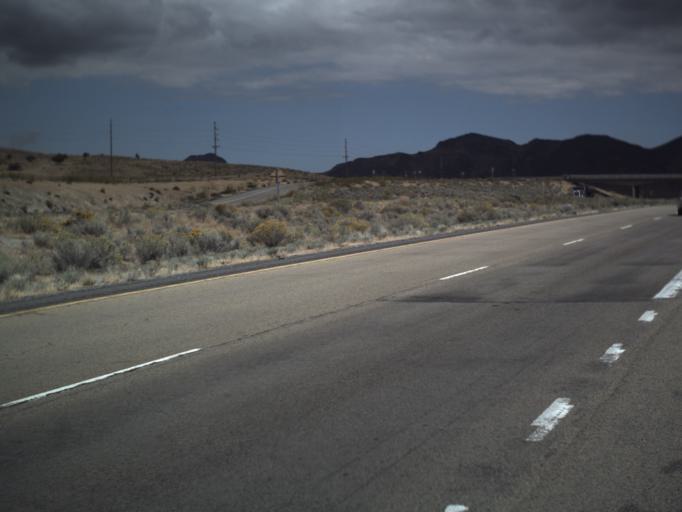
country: US
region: Utah
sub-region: Tooele County
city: Grantsville
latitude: 40.8200
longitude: -112.9073
